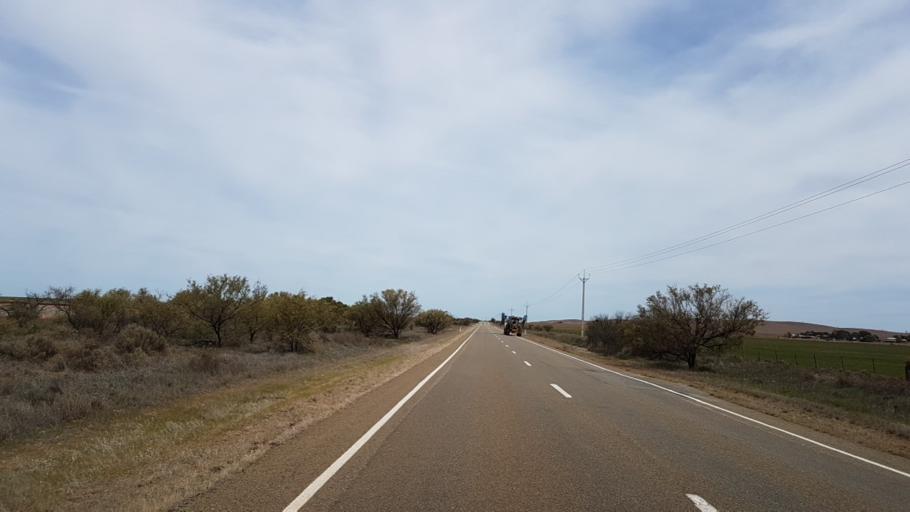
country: AU
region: South Australia
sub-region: Peterborough
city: Peterborough
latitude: -33.0054
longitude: 138.7716
